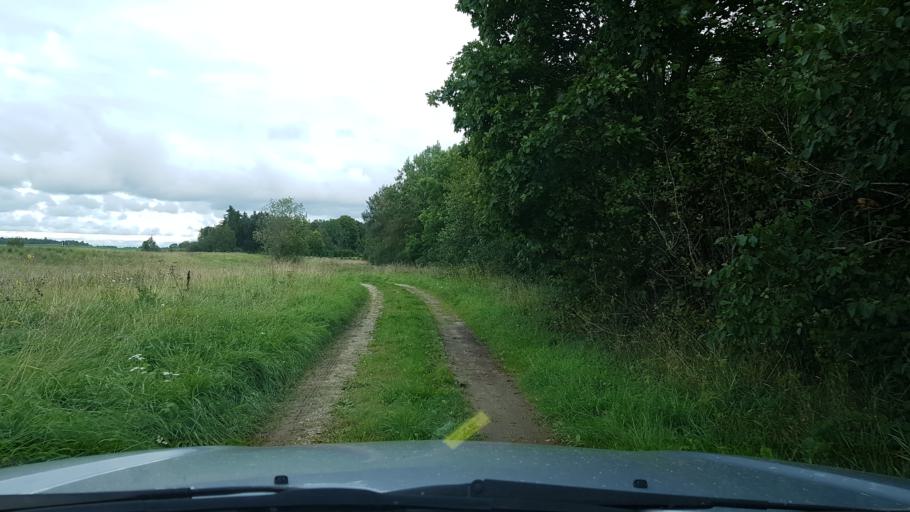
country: EE
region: Harju
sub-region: Rae vald
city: Jueri
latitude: 59.3521
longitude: 24.9509
